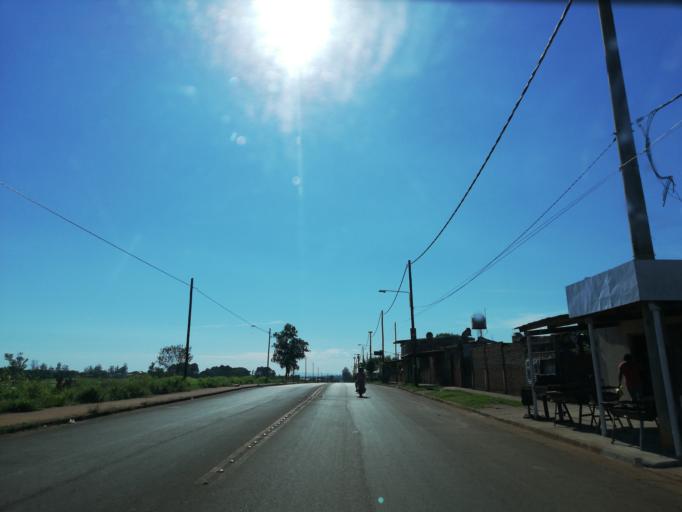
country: AR
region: Misiones
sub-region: Departamento de Capital
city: Posadas
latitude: -27.4330
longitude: -55.9405
